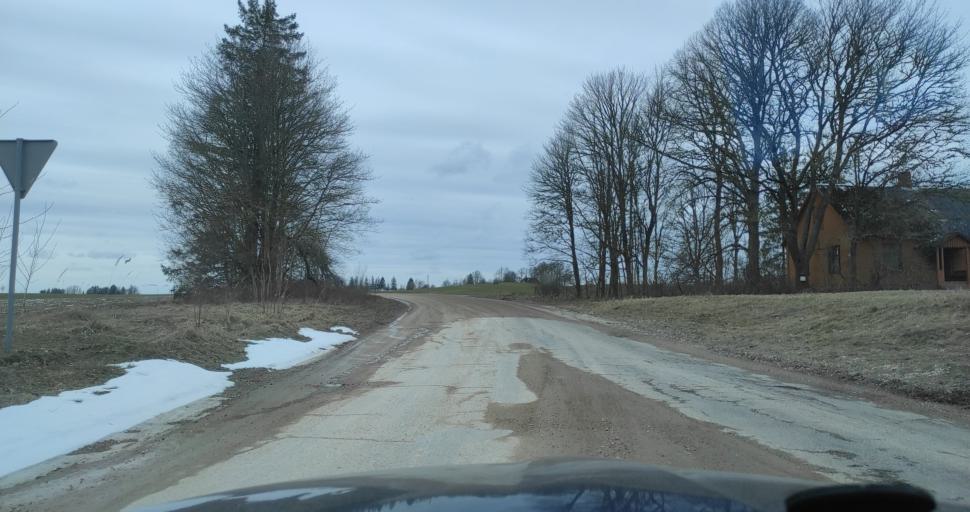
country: LV
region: Tukuma Rajons
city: Tukums
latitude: 57.0168
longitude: 23.0344
